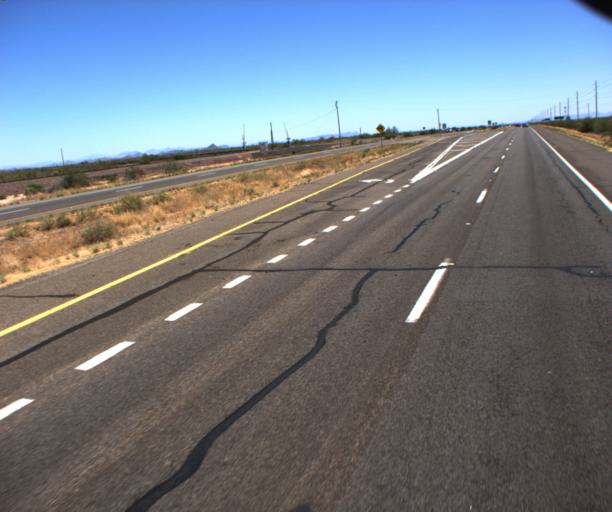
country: US
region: Arizona
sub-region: Maricopa County
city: Sun City West
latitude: 33.7570
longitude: -112.5020
